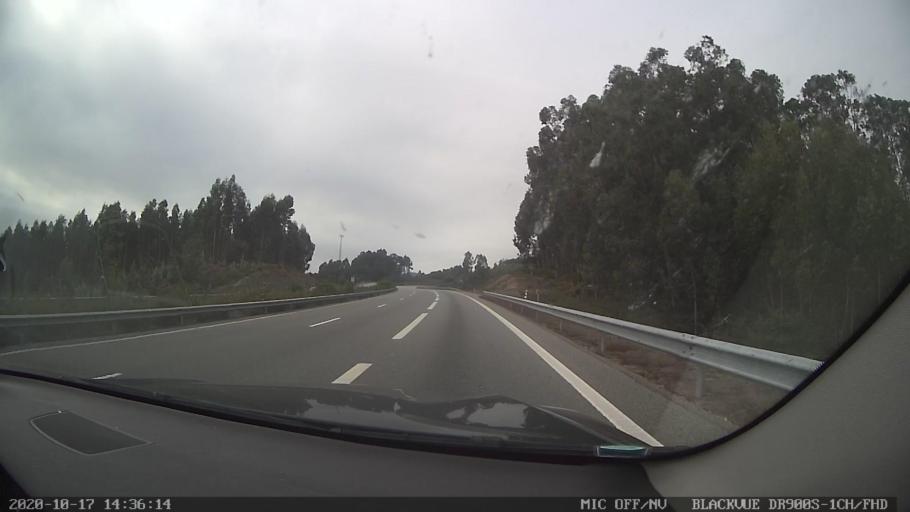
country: PT
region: Braga
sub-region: Guimaraes
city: Brito
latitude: 41.4729
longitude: -8.3796
